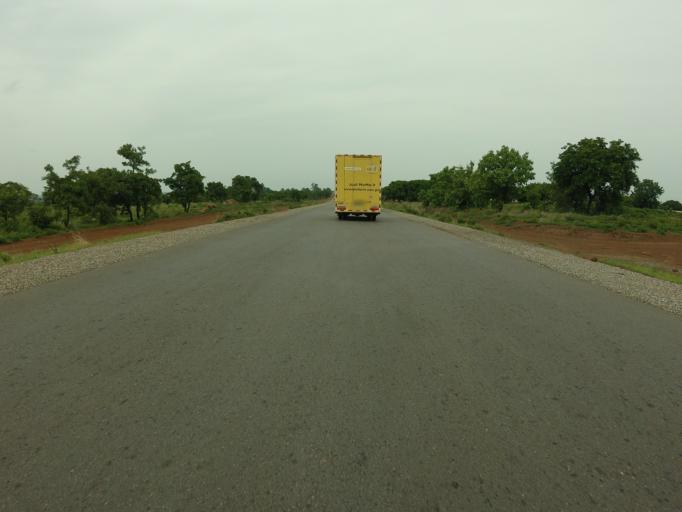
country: GH
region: Northern
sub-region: Yendi
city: Yendi
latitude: 9.3109
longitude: 0.0158
